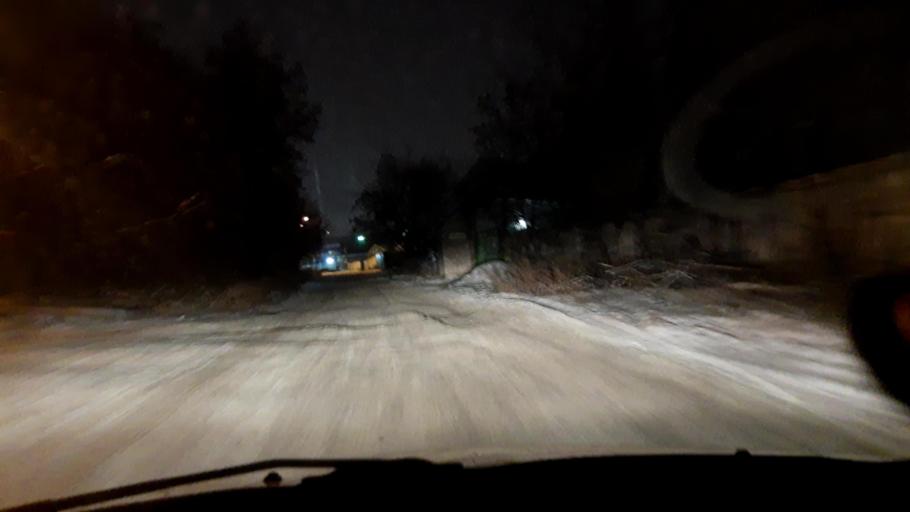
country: RU
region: Bashkortostan
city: Ufa
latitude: 54.8587
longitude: 56.0774
